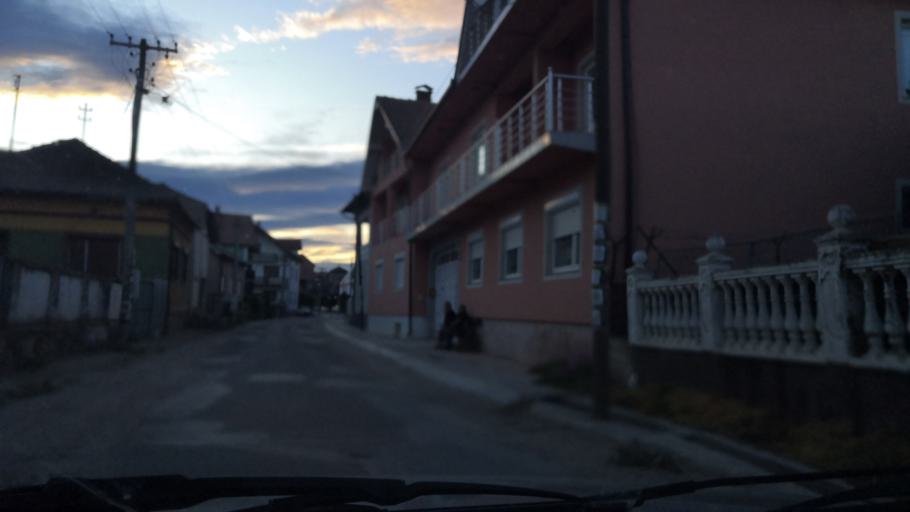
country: RO
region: Mehedinti
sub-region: Comuna Gogosu
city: Balta Verde
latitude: 44.2942
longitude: 22.5864
